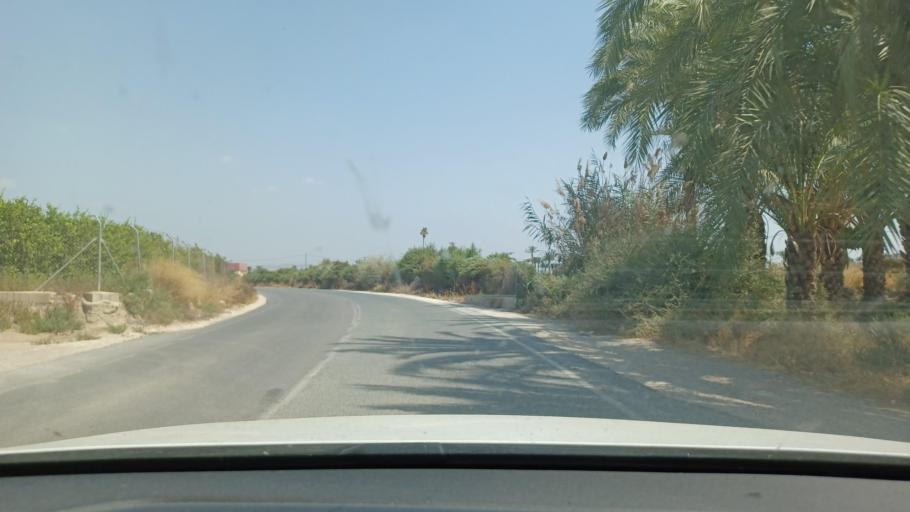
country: ES
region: Valencia
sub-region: Provincia de Alicante
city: Elche
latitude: 38.2468
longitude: -0.6909
